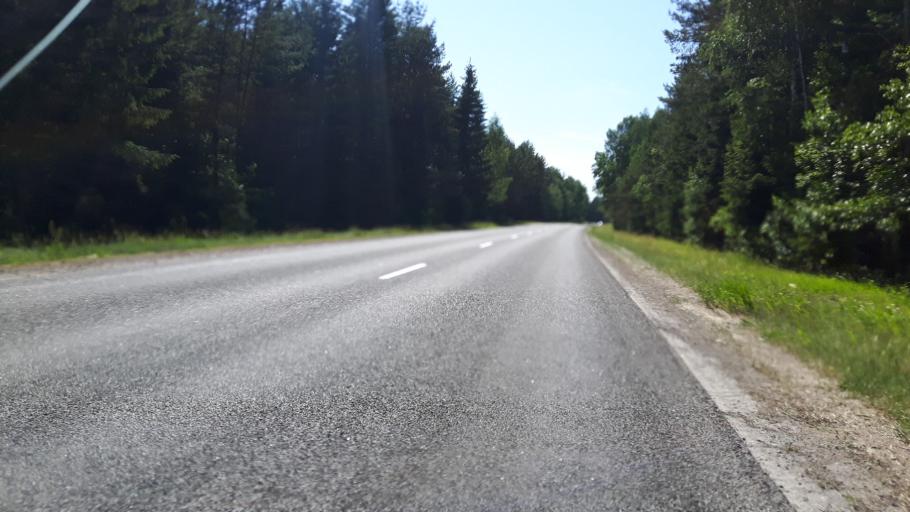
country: LV
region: Talsu Rajons
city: Stende
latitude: 57.0824
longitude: 22.4425
